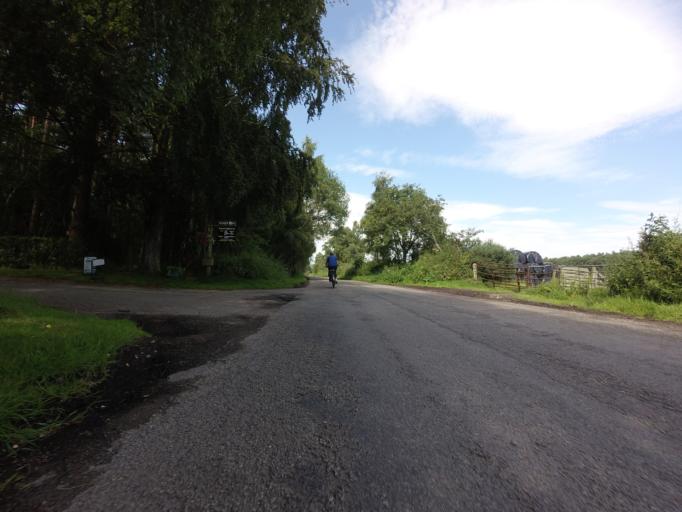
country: GB
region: Scotland
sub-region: Highland
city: Inverness
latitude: 57.5182
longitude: -4.2912
